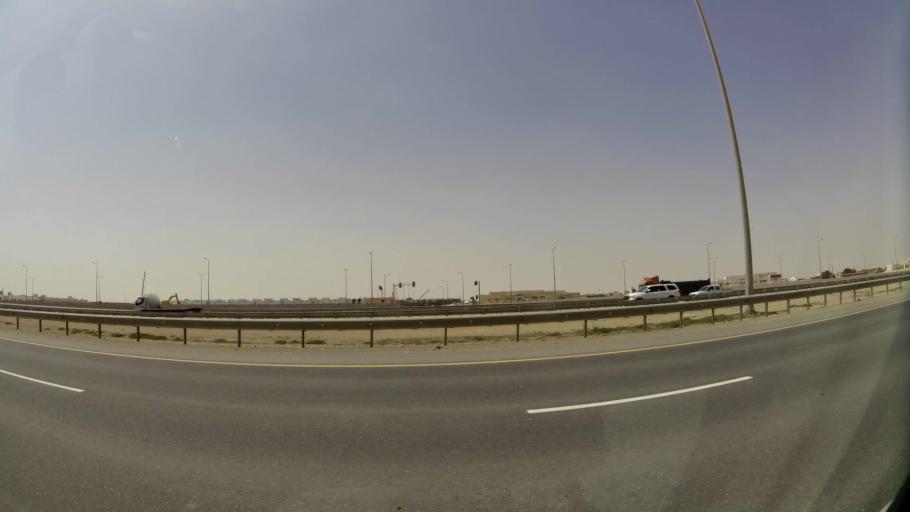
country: QA
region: Baladiyat Umm Salal
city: Umm Salal Muhammad
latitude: 25.4178
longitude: 51.4213
